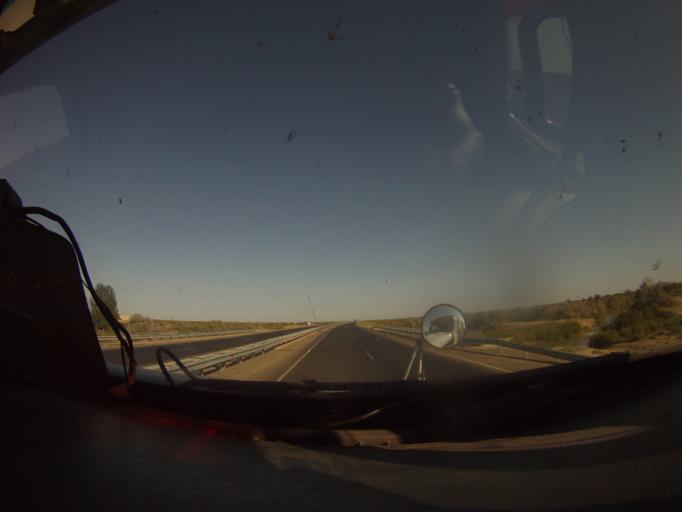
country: KZ
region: Qyzylorda
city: Belkol
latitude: 44.6683
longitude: 65.9890
